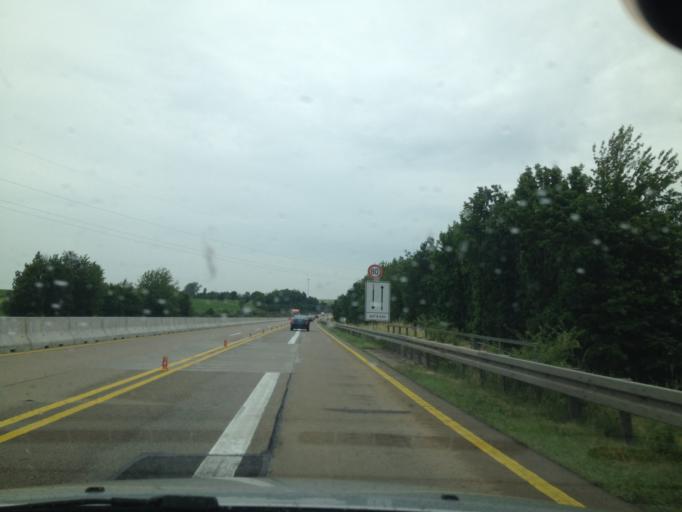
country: DE
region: Bavaria
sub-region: Regierungsbezirk Mittelfranken
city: Gollhofen
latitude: 49.5353
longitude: 10.1794
